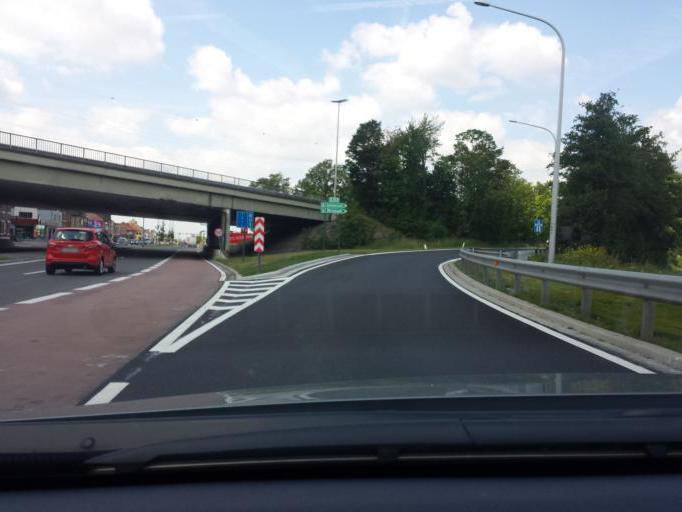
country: BE
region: Flanders
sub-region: Provincie Limburg
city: Hasselt
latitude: 50.9426
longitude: 5.2917
